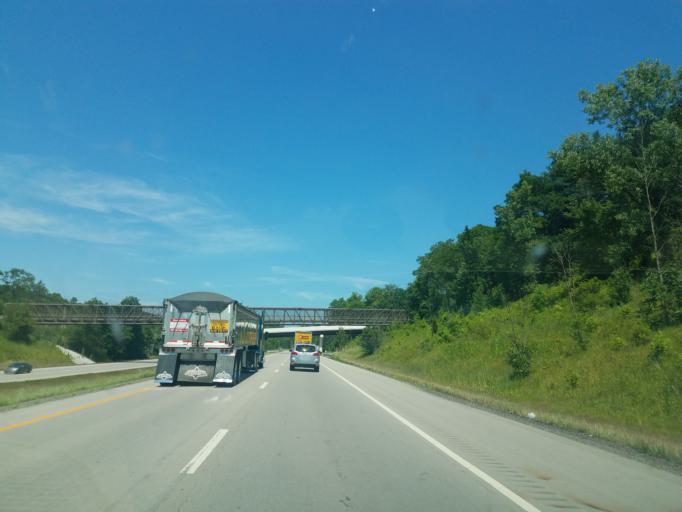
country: US
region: Ohio
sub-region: Summit County
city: Boston Heights
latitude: 41.2746
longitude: -81.5379
